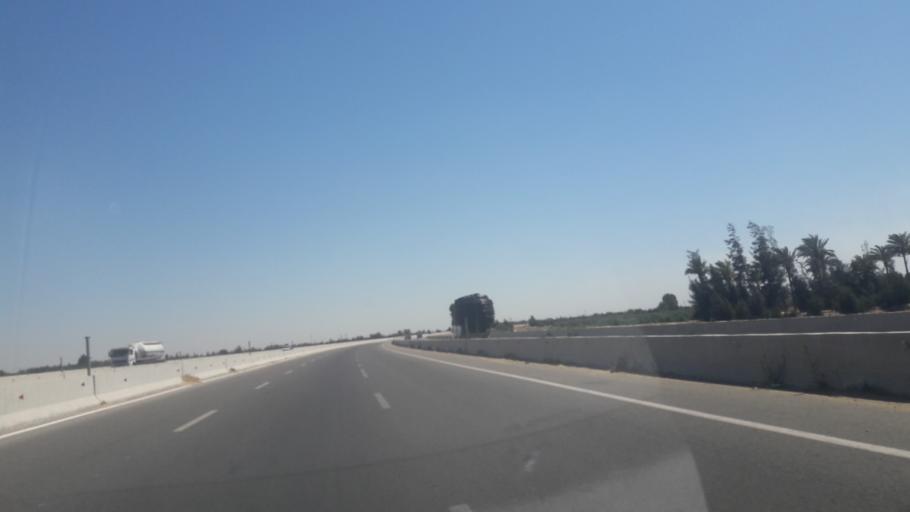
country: EG
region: Al Isma'iliyah
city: Ismailia
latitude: 30.7121
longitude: 32.1192
